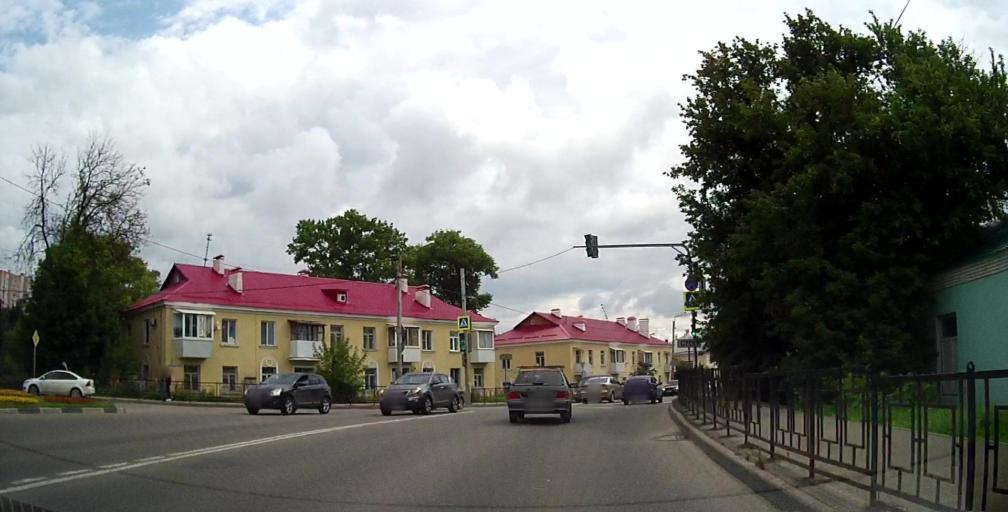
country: RU
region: Smolensk
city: Smolensk
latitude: 54.7999
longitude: 32.0349
